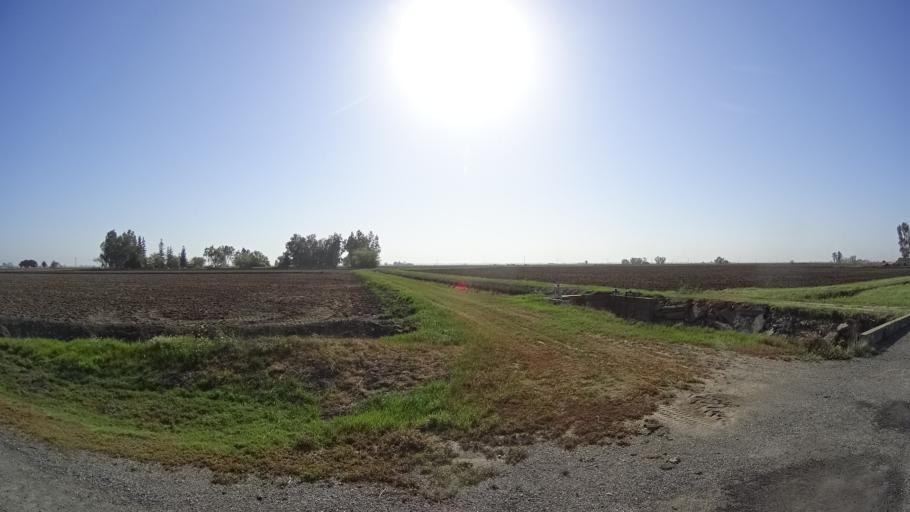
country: US
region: California
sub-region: Glenn County
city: Willows
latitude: 39.5423
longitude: -122.1035
